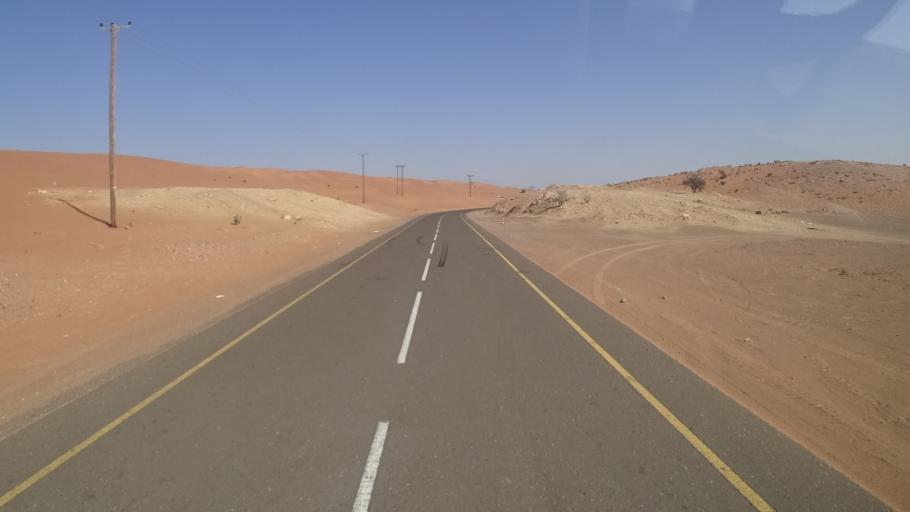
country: OM
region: Ash Sharqiyah
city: Al Qabil
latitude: 22.4809
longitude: 58.7115
